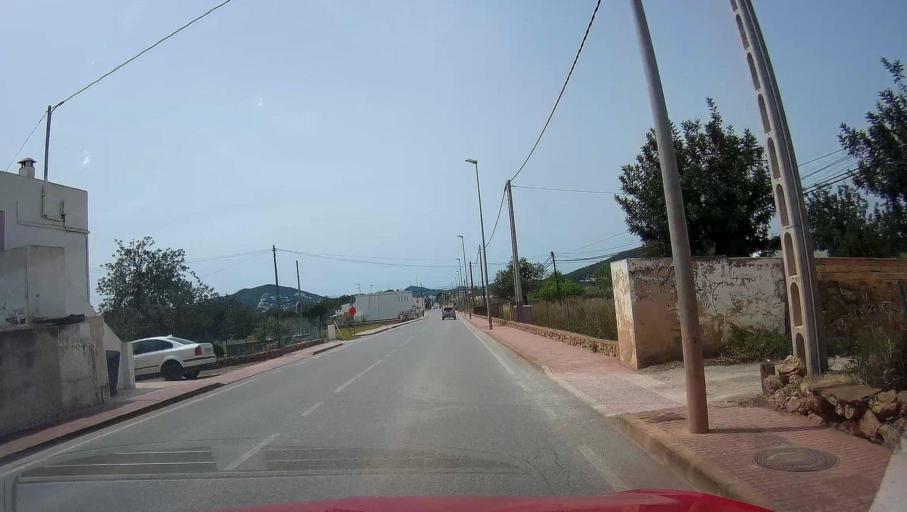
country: ES
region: Balearic Islands
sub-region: Illes Balears
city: Santa Eularia des Riu
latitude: 38.9964
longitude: 1.5557
